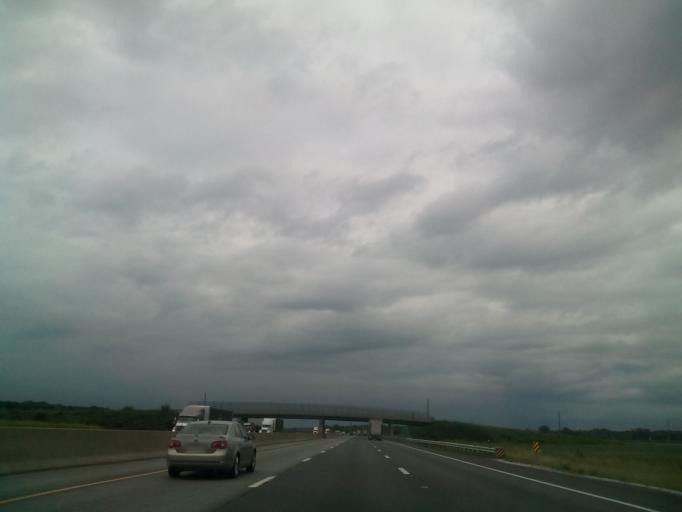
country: US
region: Ohio
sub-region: Sandusky County
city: Woodville
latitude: 41.4774
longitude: -83.3405
